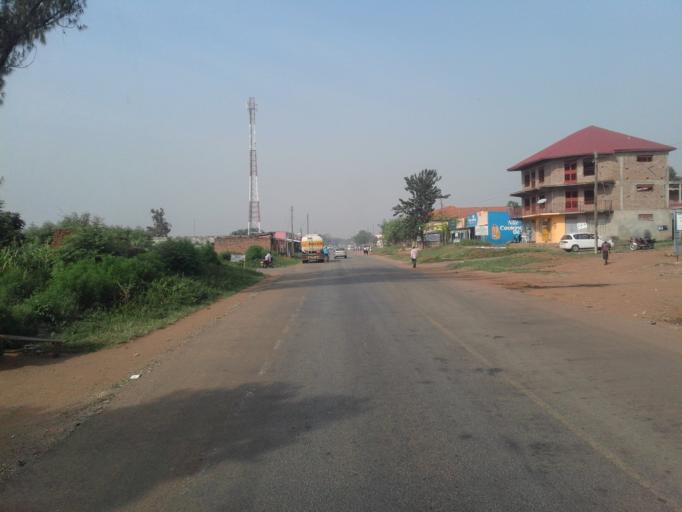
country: UG
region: Eastern Region
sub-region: Budaka District
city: Budaka
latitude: 1.0164
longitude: 33.9515
